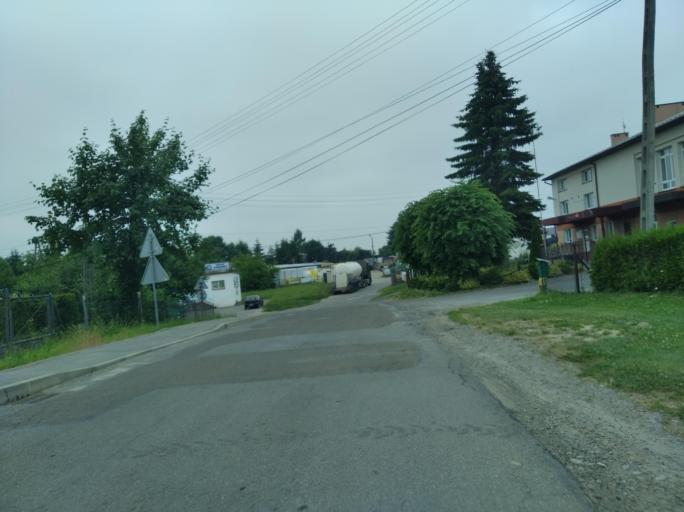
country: PL
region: Subcarpathian Voivodeship
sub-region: Powiat brzozowski
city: Jablonica Polska
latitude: 49.6999
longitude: 21.8975
